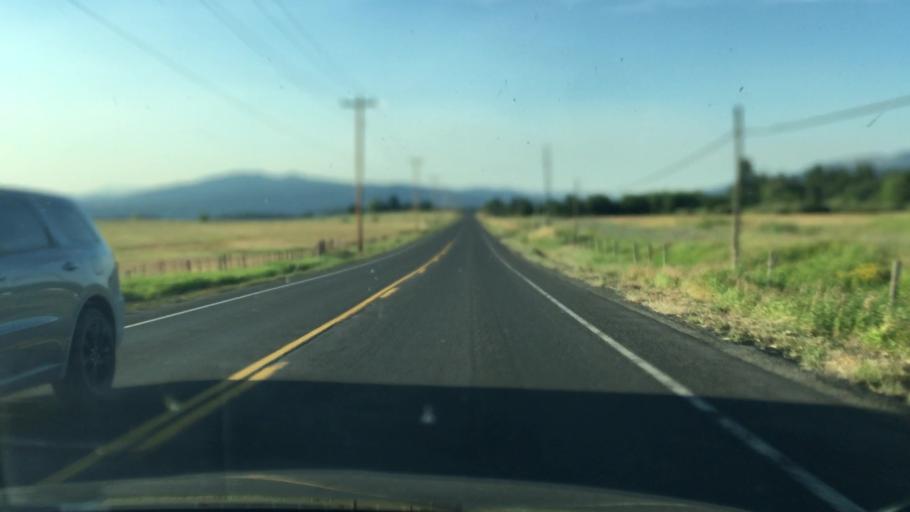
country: US
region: Idaho
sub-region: Valley County
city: McCall
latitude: 44.8730
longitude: -116.0909
